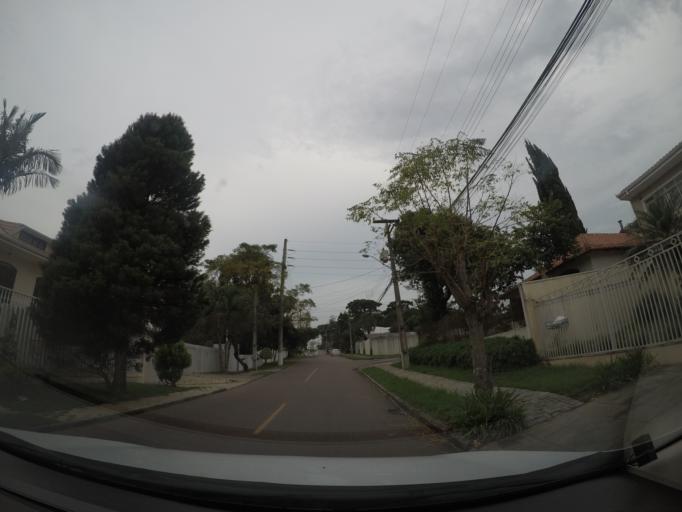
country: BR
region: Parana
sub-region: Curitiba
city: Curitiba
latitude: -25.4665
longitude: -49.2445
